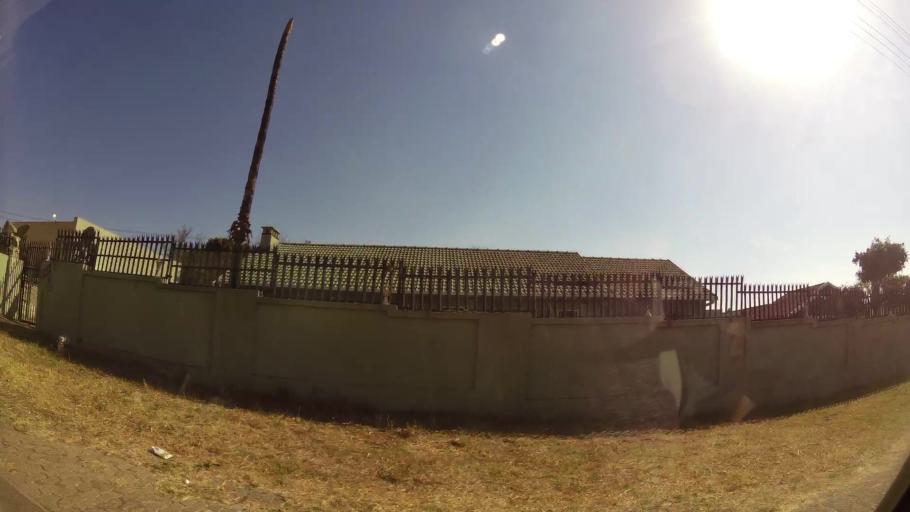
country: ZA
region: Gauteng
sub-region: City of Johannesburg Metropolitan Municipality
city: Johannesburg
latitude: -26.2530
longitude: 28.0980
